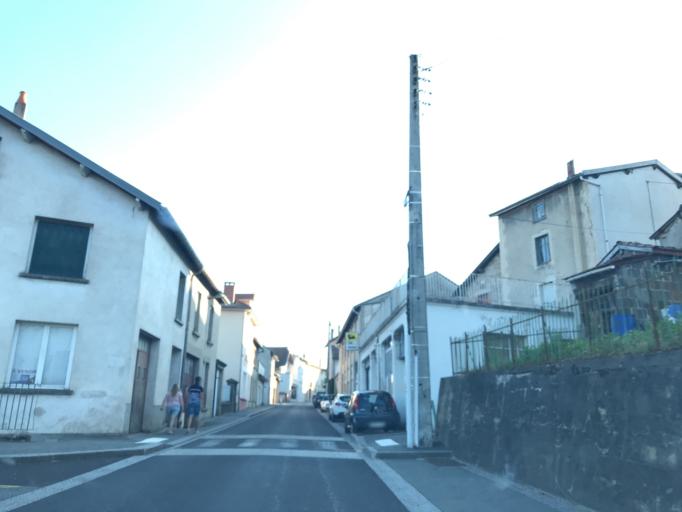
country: FR
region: Auvergne
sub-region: Departement du Puy-de-Dome
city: Saint-Remy-sur-Durolle
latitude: 45.8886
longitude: 3.5945
